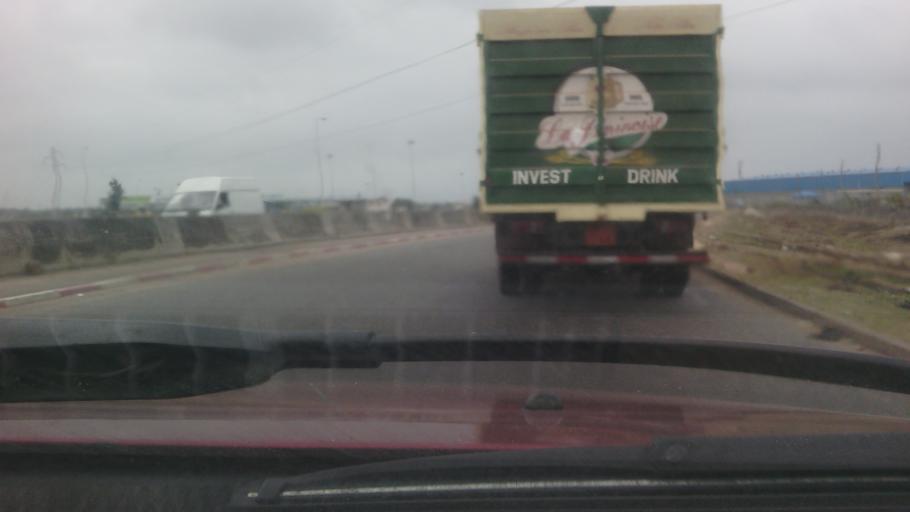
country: BJ
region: Littoral
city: Cotonou
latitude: 6.3716
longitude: 2.5325
